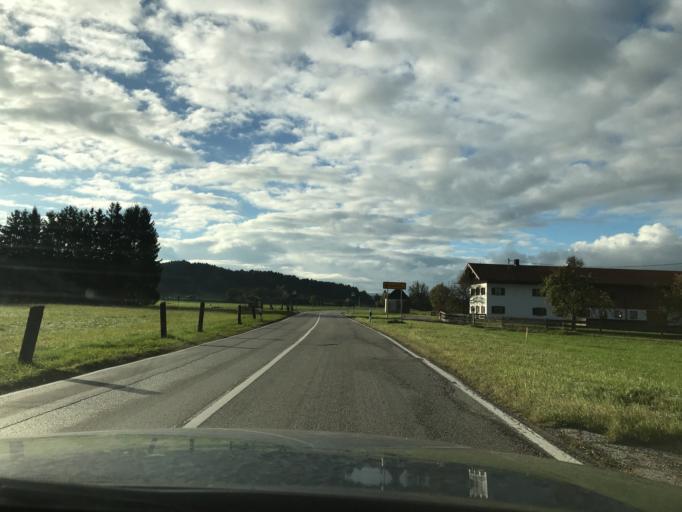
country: DE
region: Bavaria
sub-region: Upper Bavaria
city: Konigsdorf
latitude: 47.8362
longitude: 11.5301
